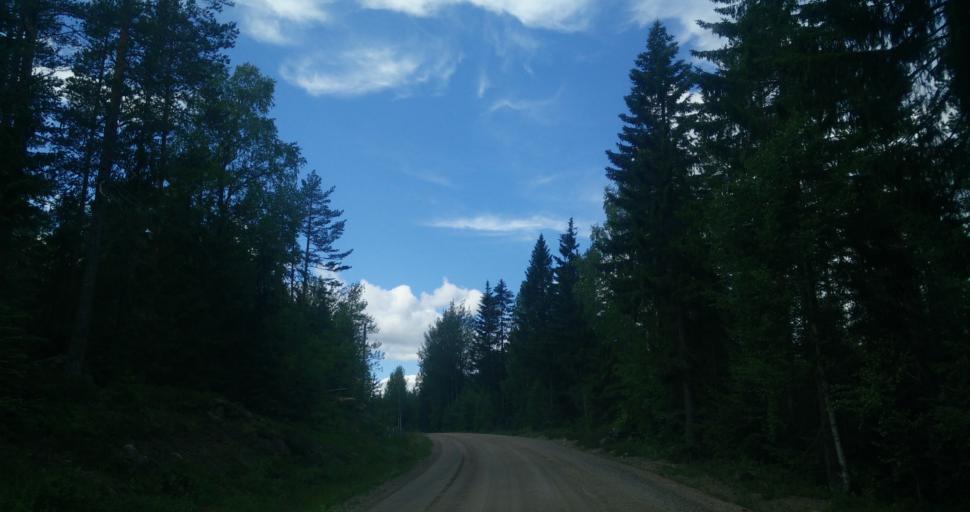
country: SE
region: Vaesternorrland
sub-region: Sundsvalls Kommun
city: Vi
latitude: 62.1472
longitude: 17.1455
